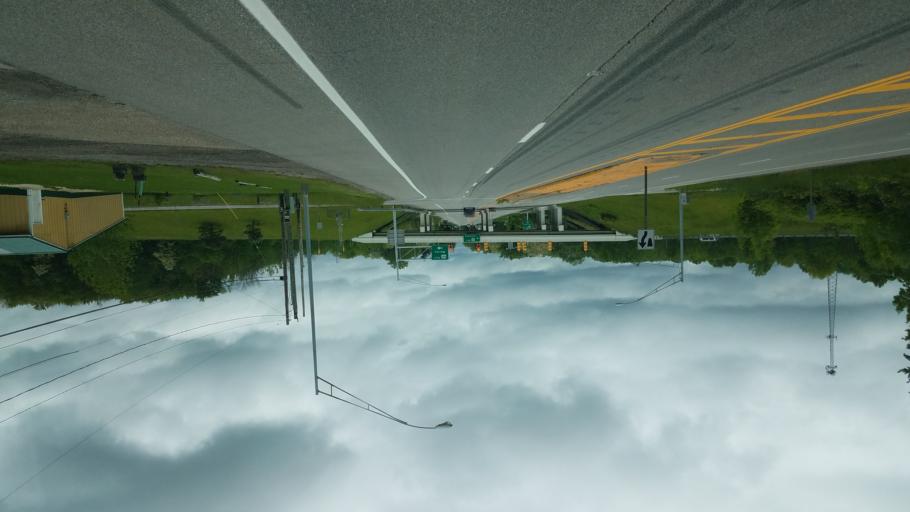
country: US
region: Ohio
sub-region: Portage County
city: Mantua
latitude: 41.3825
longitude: -81.2171
